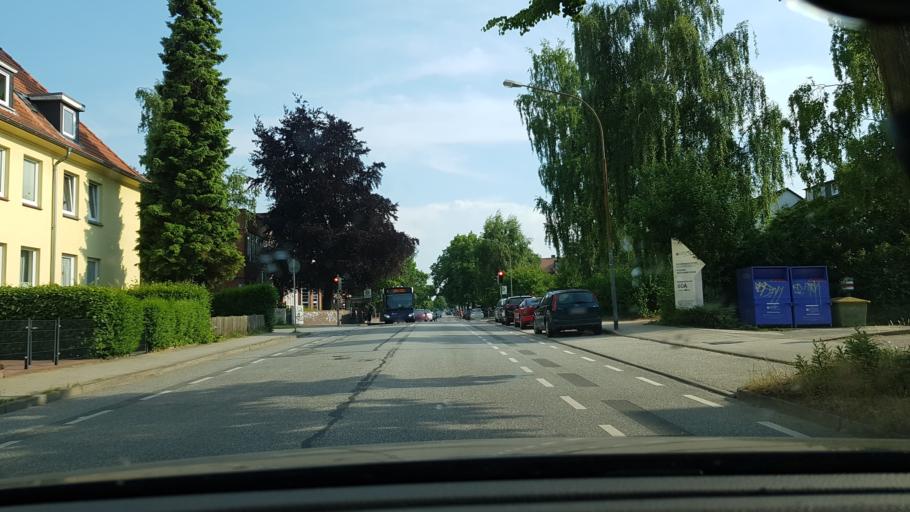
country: DE
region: Schleswig-Holstein
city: Luebeck
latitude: 53.8484
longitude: 10.6989
